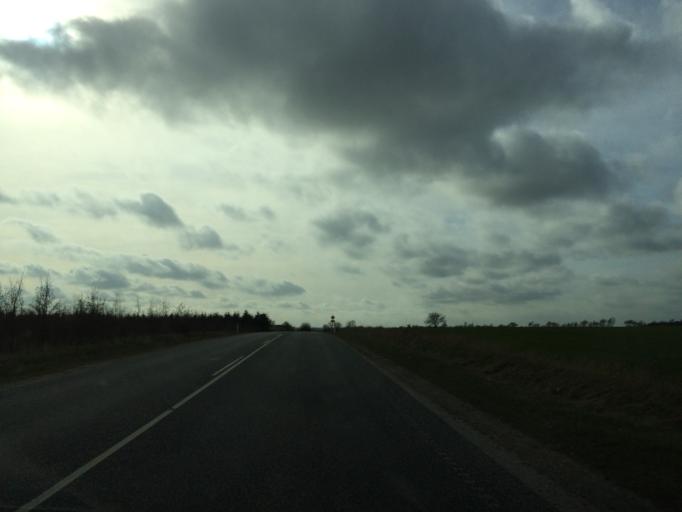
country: DK
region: Central Jutland
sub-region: Randers Kommune
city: Assentoft
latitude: 56.4419
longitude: 10.2003
